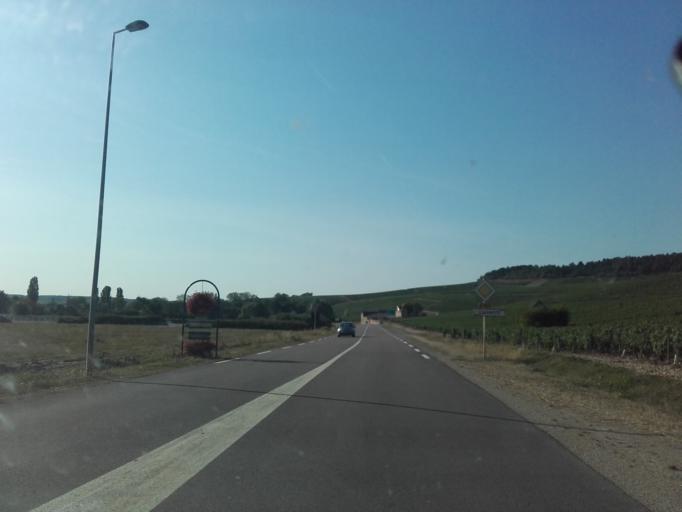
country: FR
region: Bourgogne
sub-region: Departement de l'Yonne
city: Chablis
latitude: 47.8175
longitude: 3.8069
